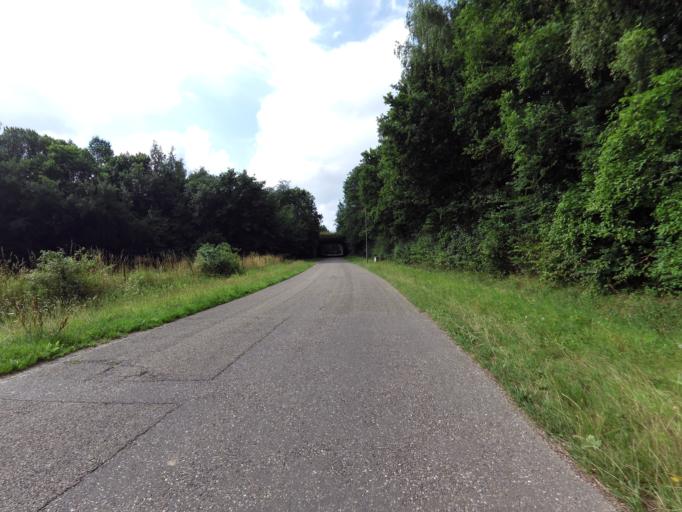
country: NL
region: Limburg
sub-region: Valkenburg aan de Geul
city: Valkenburg
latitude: 50.8812
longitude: 5.8345
